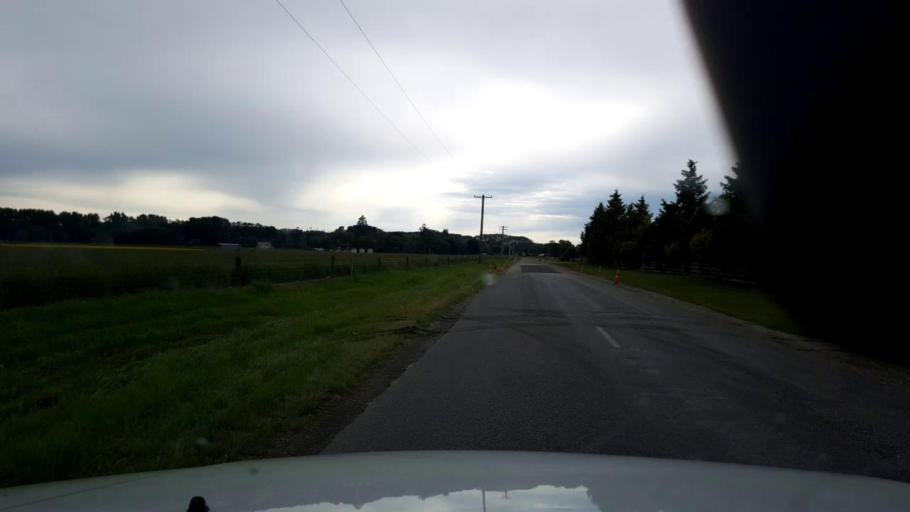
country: NZ
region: Canterbury
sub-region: Timaru District
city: Pleasant Point
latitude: -44.2709
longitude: 171.2575
